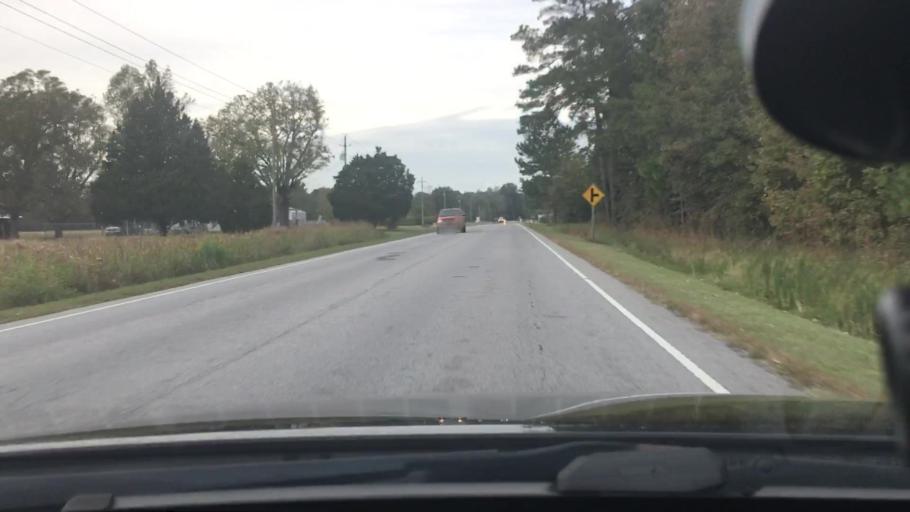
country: US
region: North Carolina
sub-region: Pitt County
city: Windsor
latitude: 35.4293
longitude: -77.2617
